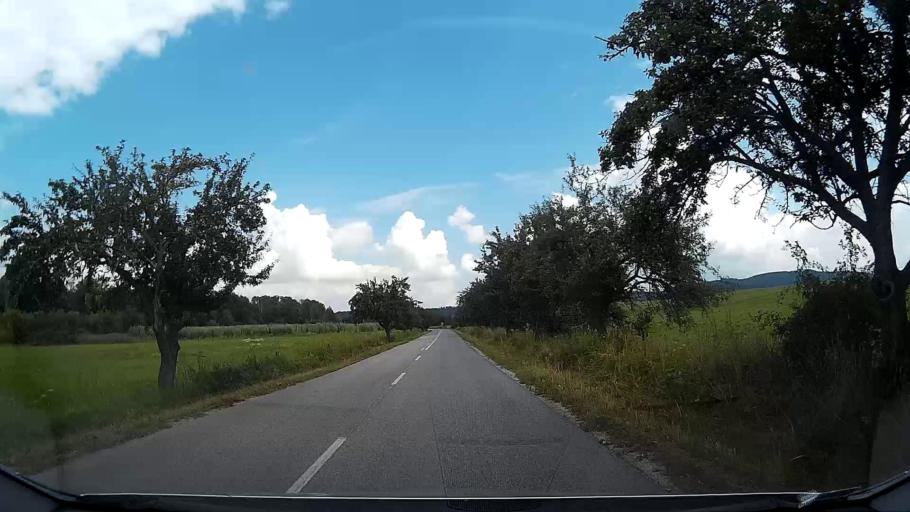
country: SK
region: Presovsky
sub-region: Okres Poprad
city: Poprad
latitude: 48.9862
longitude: 20.3867
